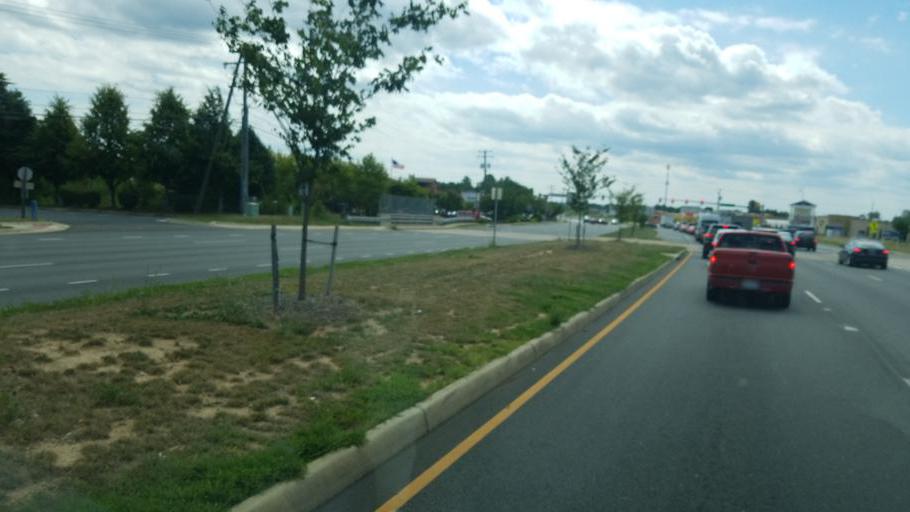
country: US
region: Virginia
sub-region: Stafford County
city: Falmouth
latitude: 38.3599
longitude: -77.5192
